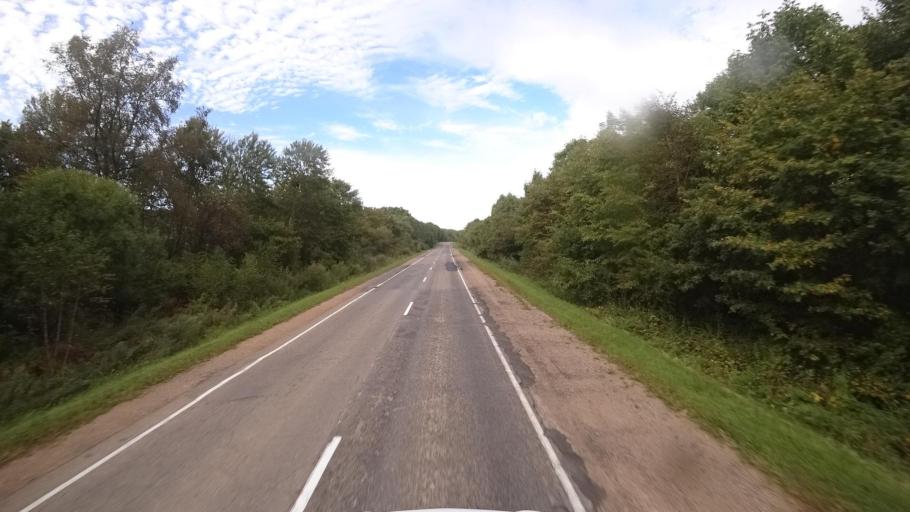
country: RU
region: Primorskiy
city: Dostoyevka
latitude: 44.3498
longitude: 133.4182
